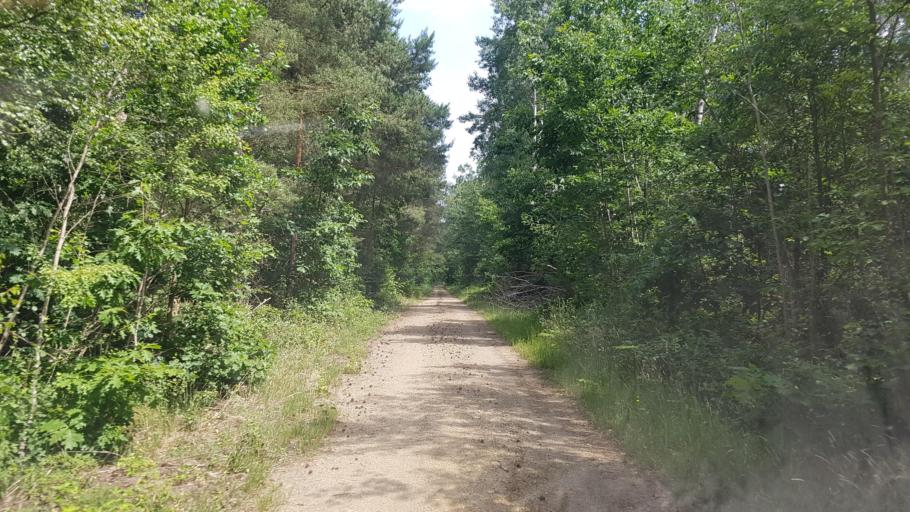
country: DE
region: Brandenburg
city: Plessa
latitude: 51.4980
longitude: 13.6365
